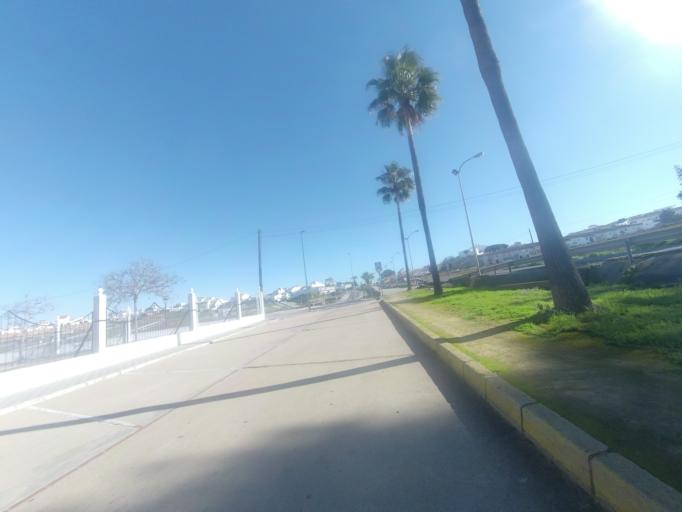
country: ES
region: Andalusia
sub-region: Provincia de Huelva
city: Palos de la Frontera
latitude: 37.2241
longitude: -6.8949
